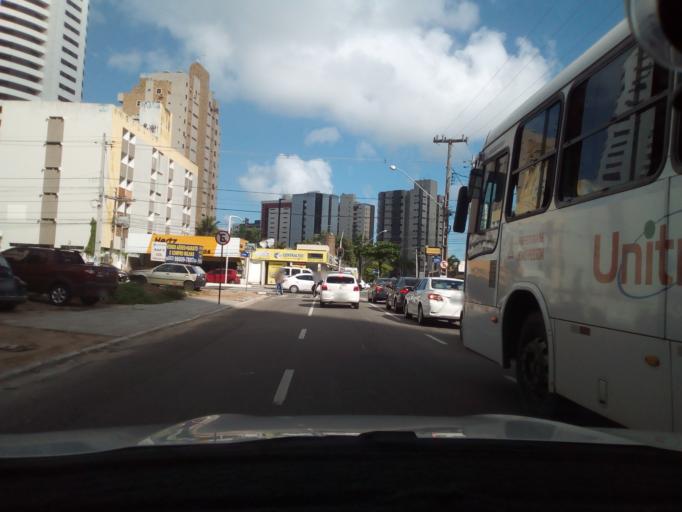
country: BR
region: Paraiba
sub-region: Joao Pessoa
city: Joao Pessoa
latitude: -7.1119
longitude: -34.8287
